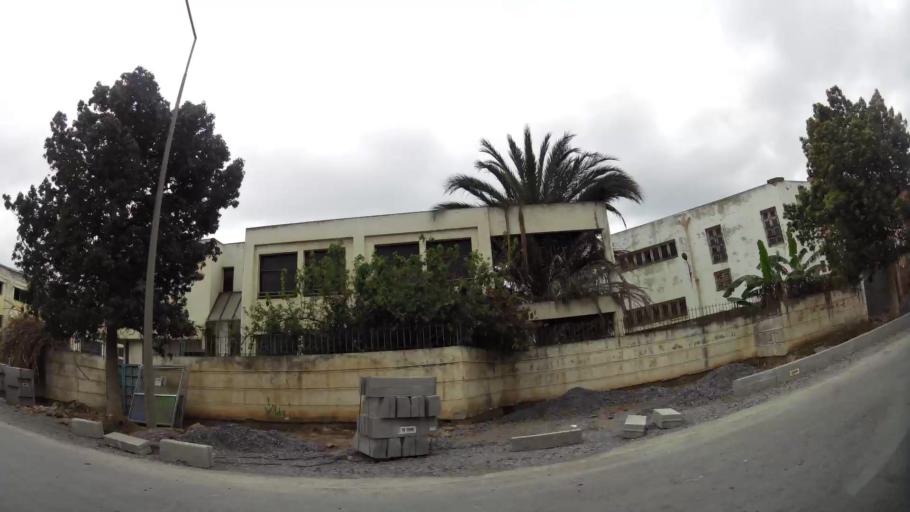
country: MA
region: Rabat-Sale-Zemmour-Zaer
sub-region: Rabat
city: Rabat
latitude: 33.9886
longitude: -6.8033
